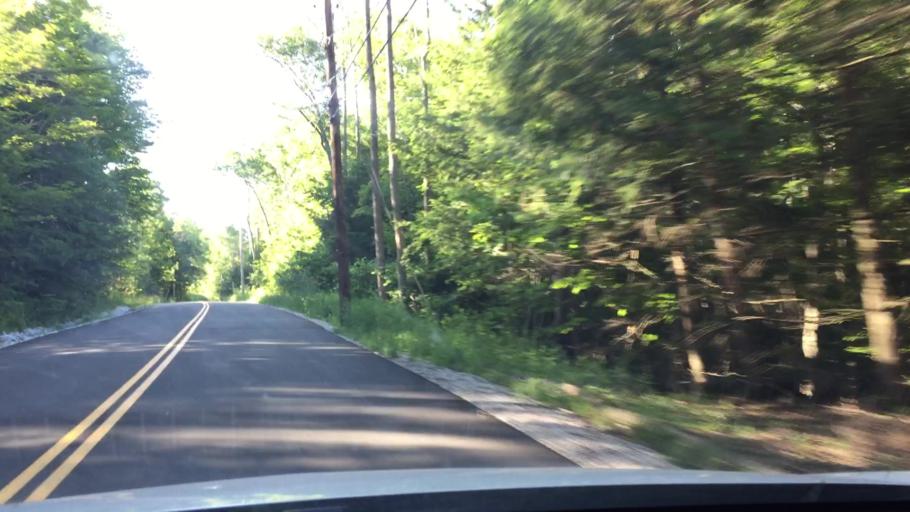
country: US
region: Massachusetts
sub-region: Berkshire County
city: Lee
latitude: 42.2826
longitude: -73.2119
